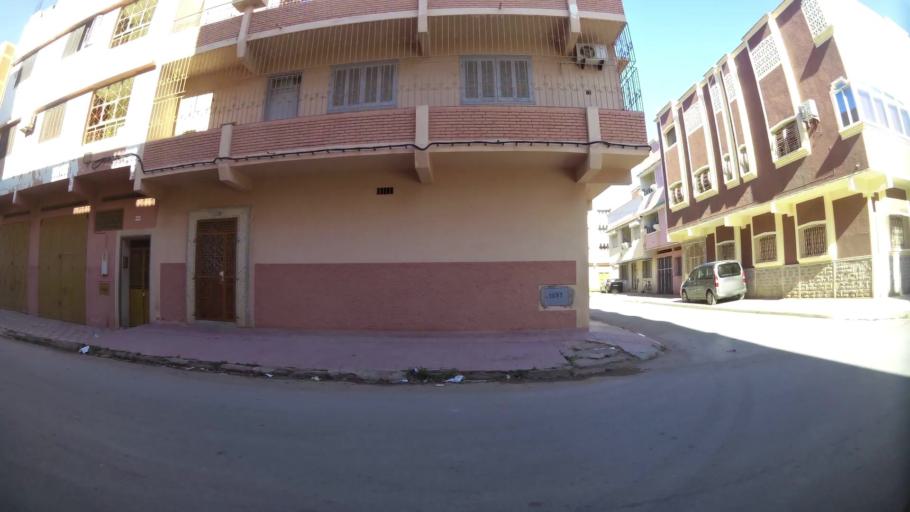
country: MA
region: Oriental
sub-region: Berkane-Taourirt
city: Berkane
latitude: 34.9333
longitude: -2.3327
